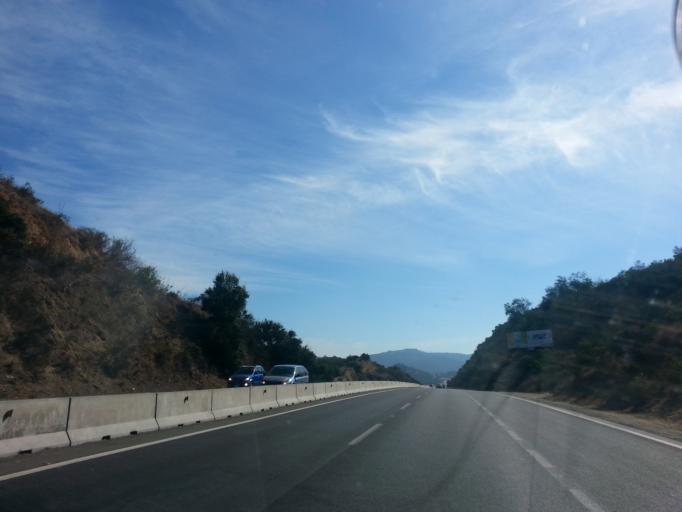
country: CL
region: Valparaiso
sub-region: Provincia de Marga Marga
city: Quilpue
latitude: -33.2841
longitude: -71.4261
